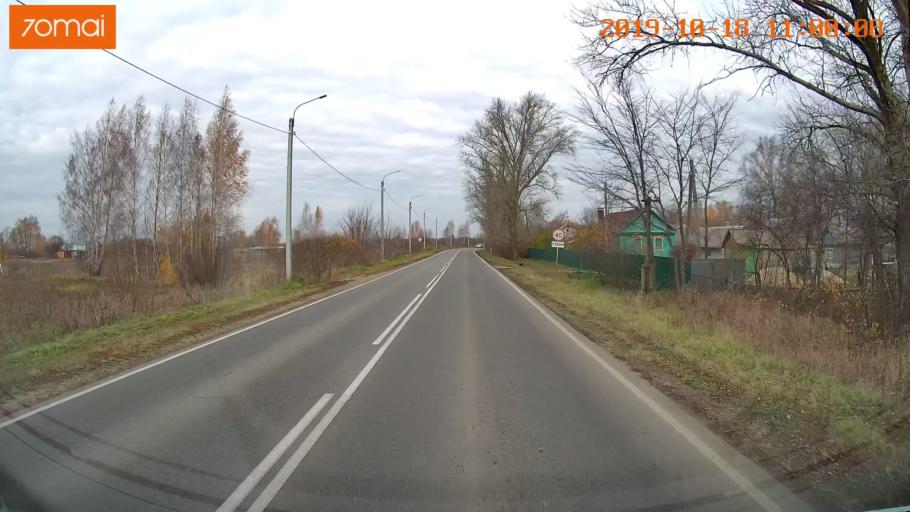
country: RU
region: Tula
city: Yepifan'
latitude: 53.8394
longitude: 38.5534
